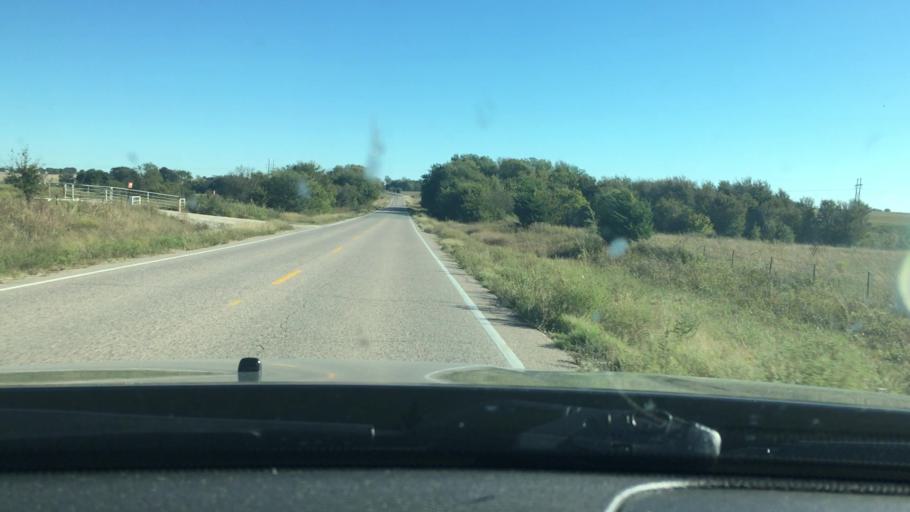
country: US
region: Oklahoma
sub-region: Marshall County
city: Madill
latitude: 34.1098
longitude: -96.7441
